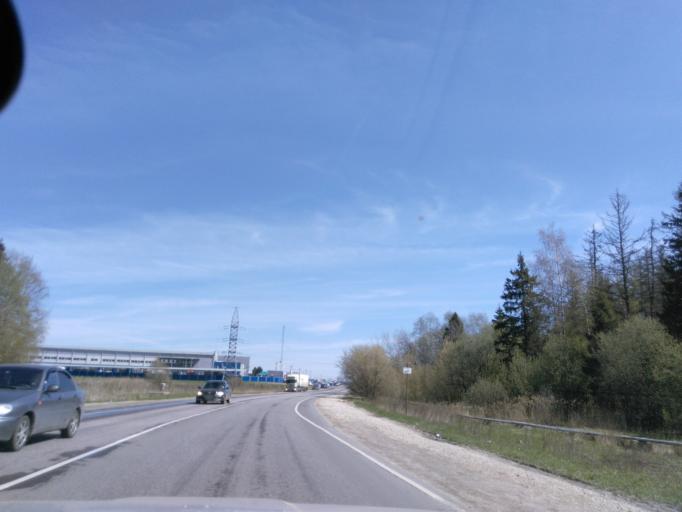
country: RU
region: Moskovskaya
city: Rzhavki
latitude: 55.9832
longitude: 37.2697
